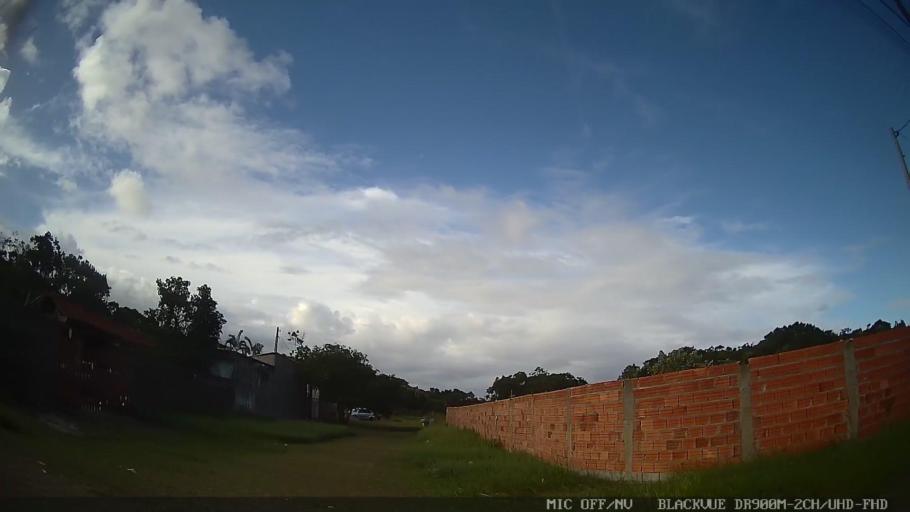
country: BR
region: Sao Paulo
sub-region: Itanhaem
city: Itanhaem
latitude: -24.2033
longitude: -46.8558
